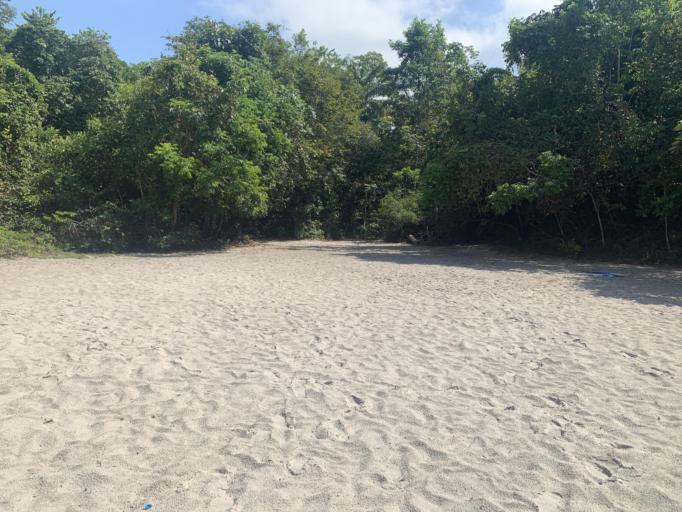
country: BR
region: Amazonas
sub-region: Manaus
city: Manaus
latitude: -3.0978
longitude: -59.9540
